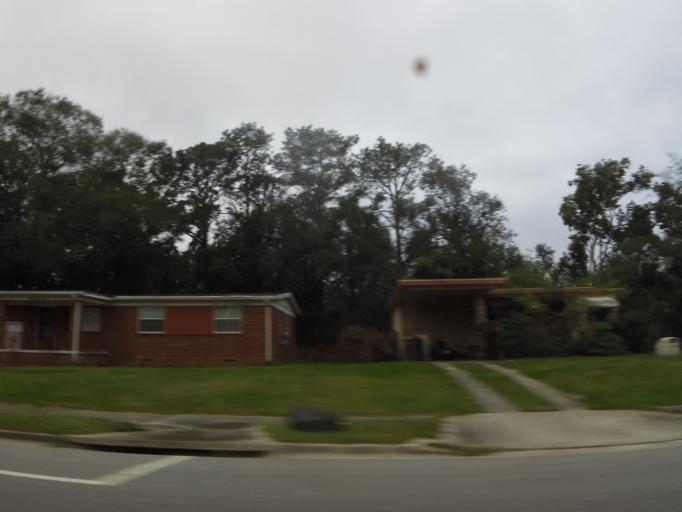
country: US
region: Florida
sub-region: Clay County
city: Bellair-Meadowbrook Terrace
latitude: 30.2685
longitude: -81.7475
